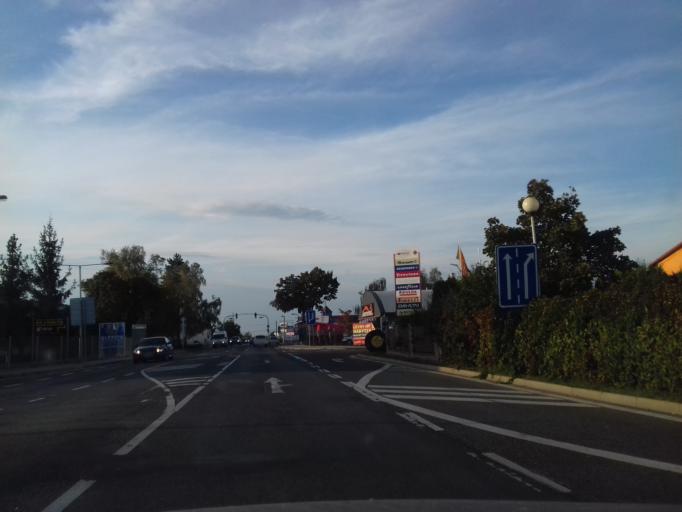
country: CZ
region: Central Bohemia
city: Vestec
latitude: 49.9847
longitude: 14.4948
